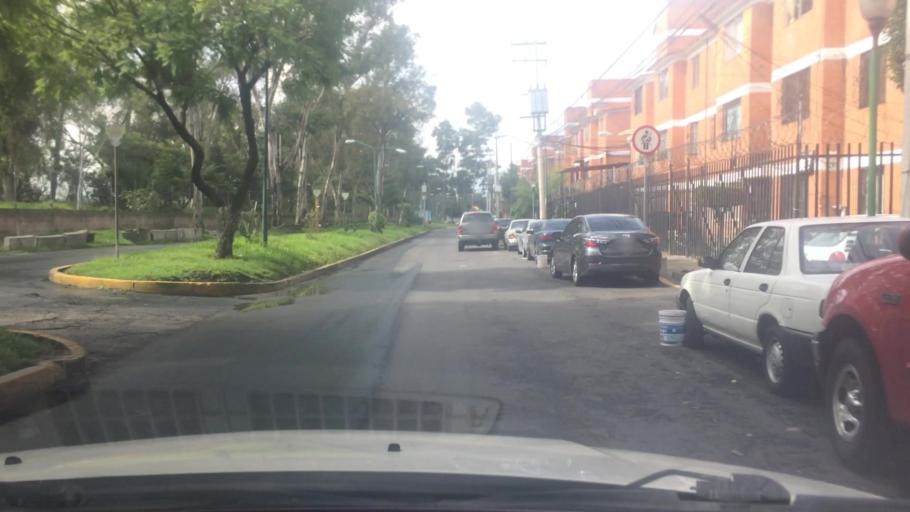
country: MX
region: Mexico City
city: Xochimilco
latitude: 19.3091
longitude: -99.1002
